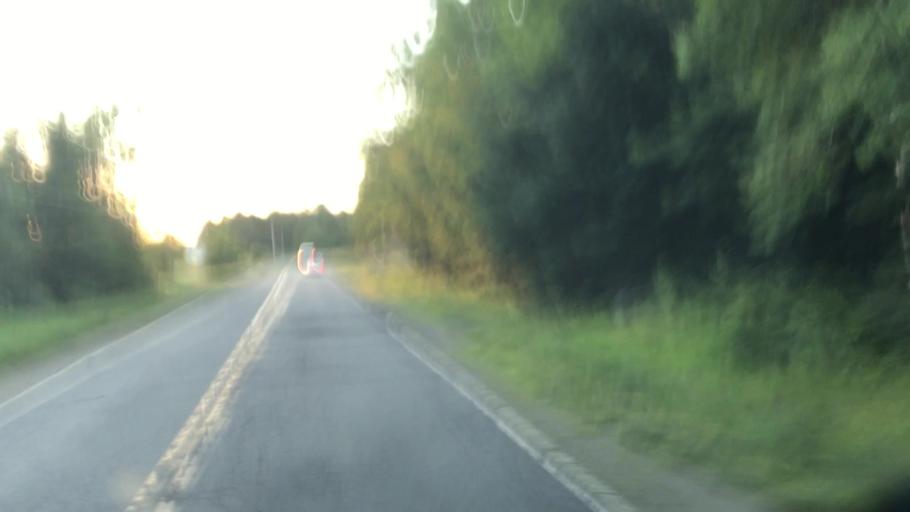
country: US
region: Maine
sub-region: Penobscot County
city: Medway
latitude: 45.6052
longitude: -68.2542
